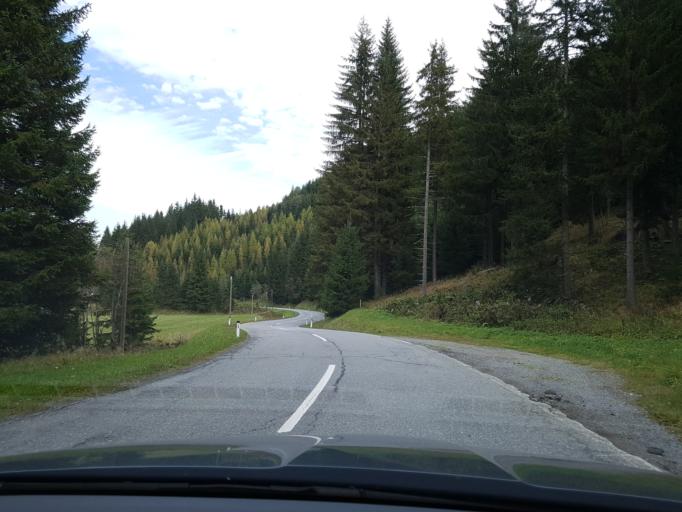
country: AT
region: Salzburg
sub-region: Politischer Bezirk Tamsweg
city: Ramingstein
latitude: 47.0169
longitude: 13.8987
